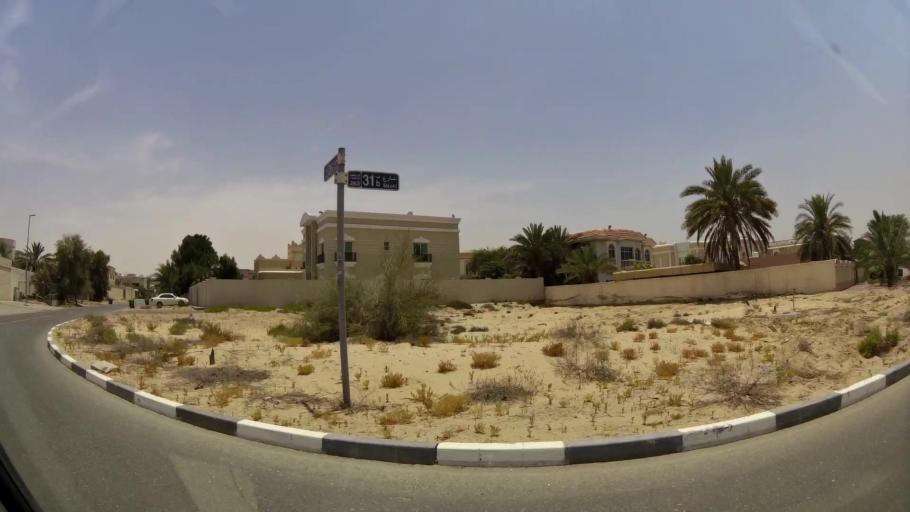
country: AE
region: Ash Shariqah
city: Sharjah
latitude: 25.2502
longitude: 55.4679
